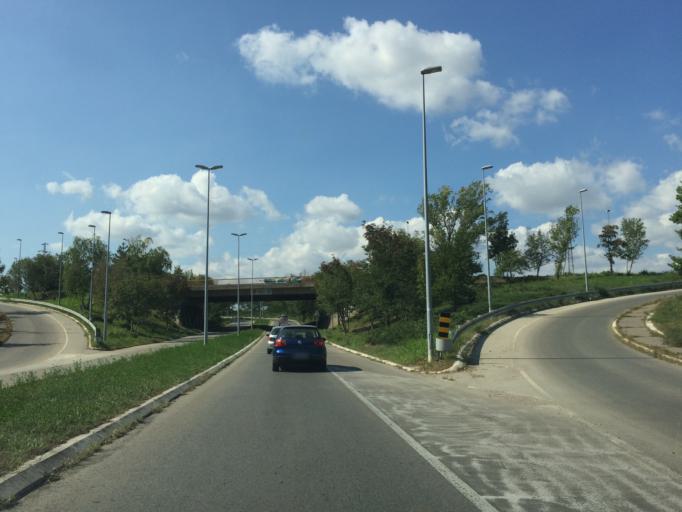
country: RS
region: Autonomna Pokrajina Vojvodina
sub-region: Juznobacki Okrug
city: Petrovaradin
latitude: 45.2284
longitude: 19.8563
